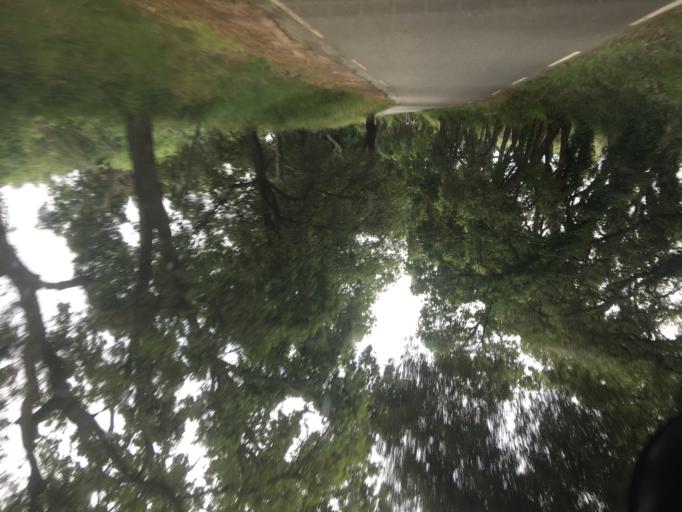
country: FR
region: Provence-Alpes-Cote d'Azur
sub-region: Departement du Var
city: La Londe-les-Maures
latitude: 43.1557
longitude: 6.2248
